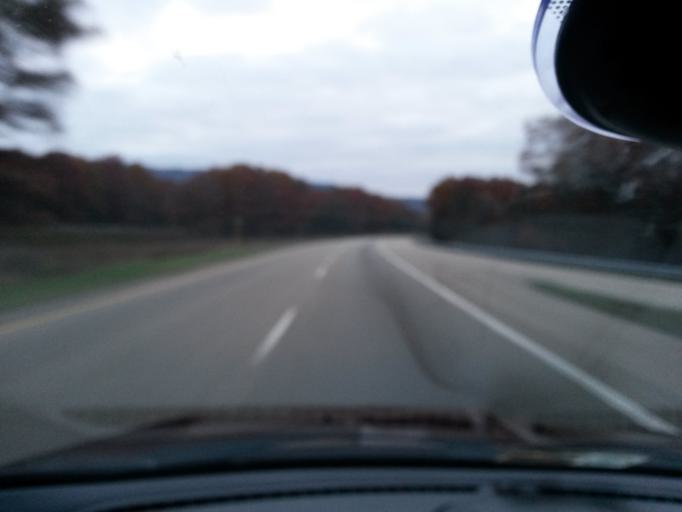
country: US
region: Virginia
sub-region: Alleghany County
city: Clifton Forge
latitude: 37.8298
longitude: -79.7559
